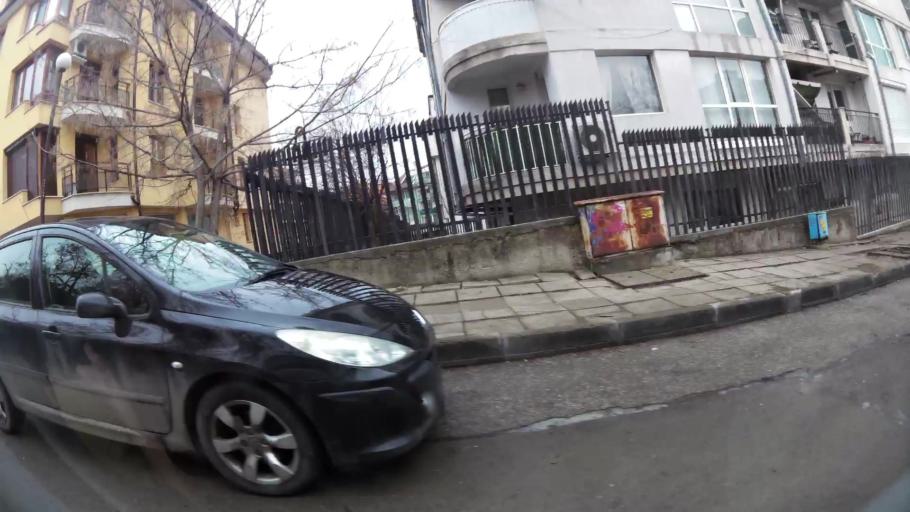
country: BG
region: Sofia-Capital
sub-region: Stolichna Obshtina
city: Sofia
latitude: 42.6689
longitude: 23.2452
